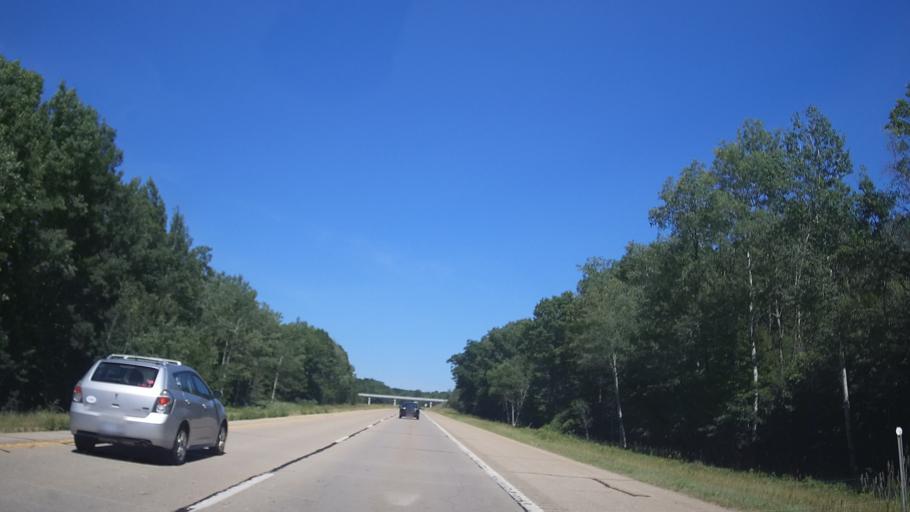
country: US
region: Michigan
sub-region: Clare County
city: Clare
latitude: 43.8714
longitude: -84.8361
